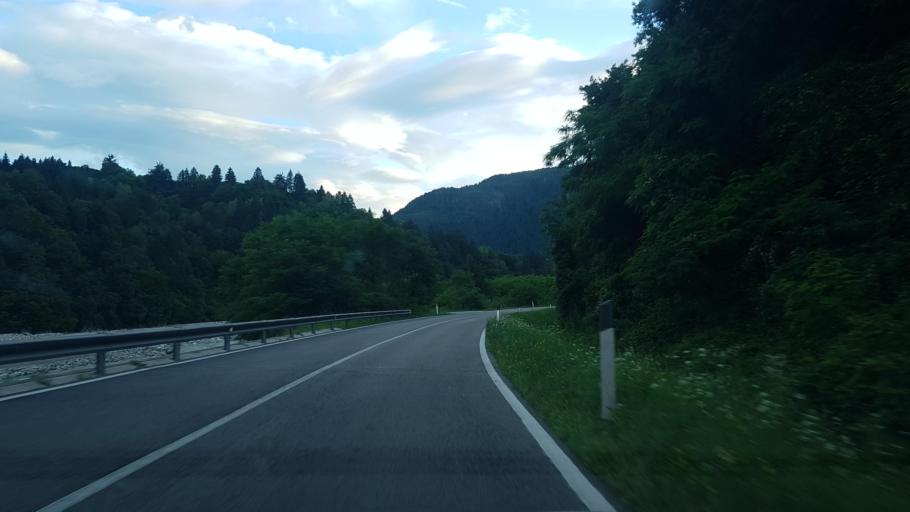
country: IT
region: Friuli Venezia Giulia
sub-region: Provincia di Udine
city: Zuglio
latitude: 46.4598
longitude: 13.0434
